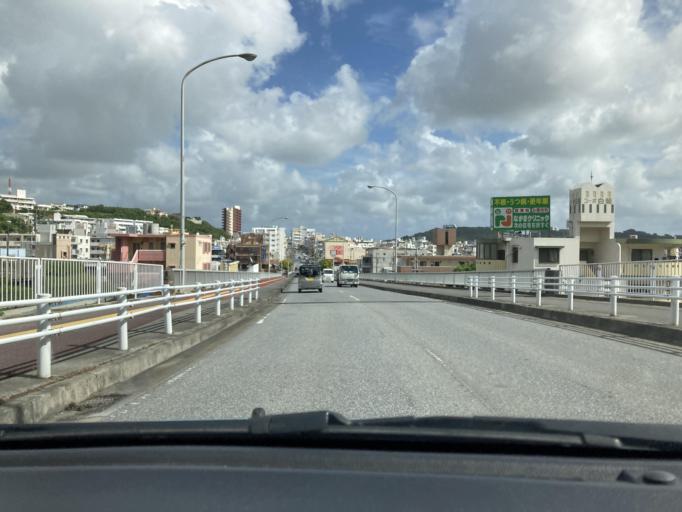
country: JP
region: Okinawa
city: Tomigusuku
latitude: 26.1851
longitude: 127.6741
